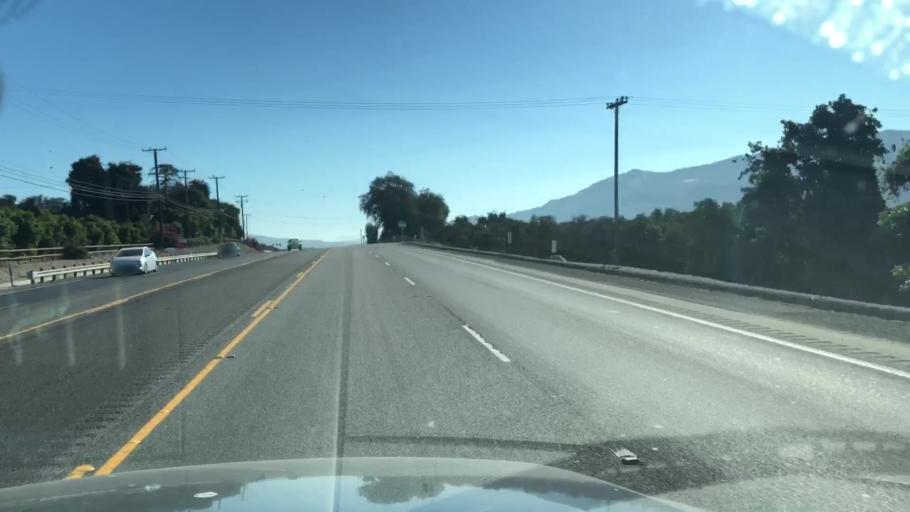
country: US
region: California
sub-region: Ventura County
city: Fillmore
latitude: 34.3961
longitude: -118.8633
